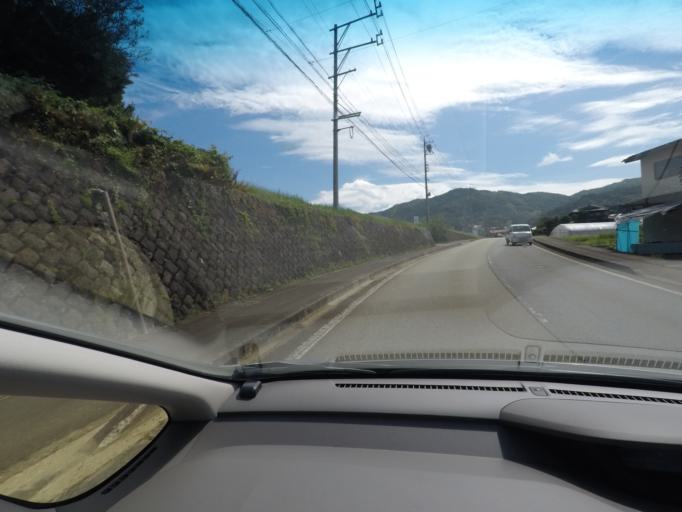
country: JP
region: Gifu
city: Takayama
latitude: 36.1375
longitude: 137.2894
